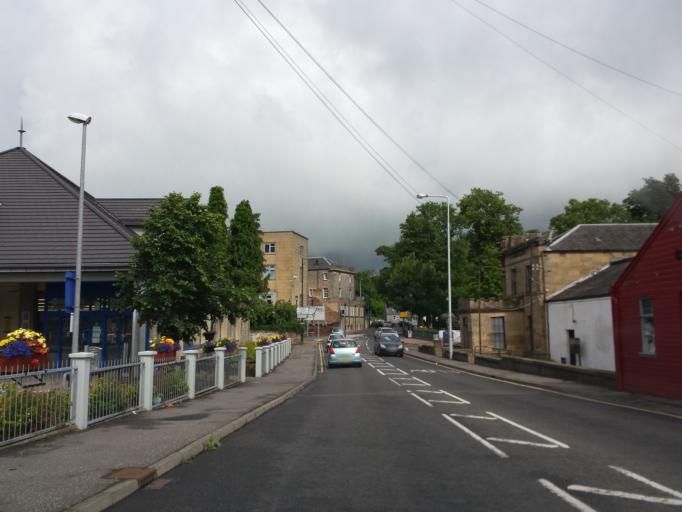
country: GB
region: Scotland
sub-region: Fife
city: Cupar
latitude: 56.3184
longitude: -3.0081
